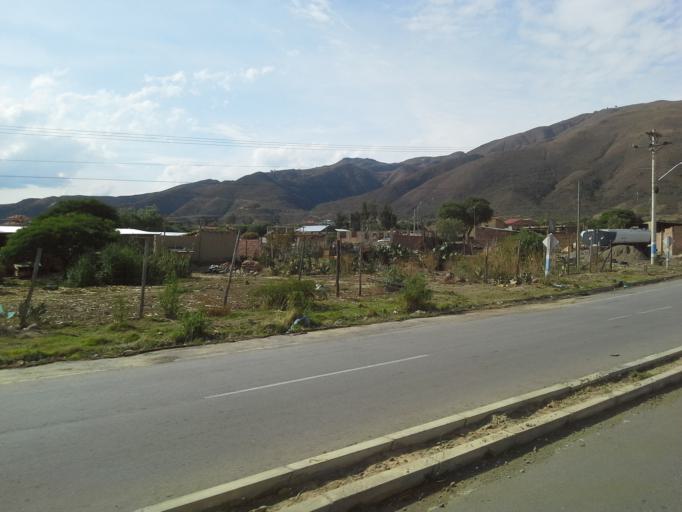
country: BO
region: Cochabamba
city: Tarata
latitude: -17.5457
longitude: -66.0058
